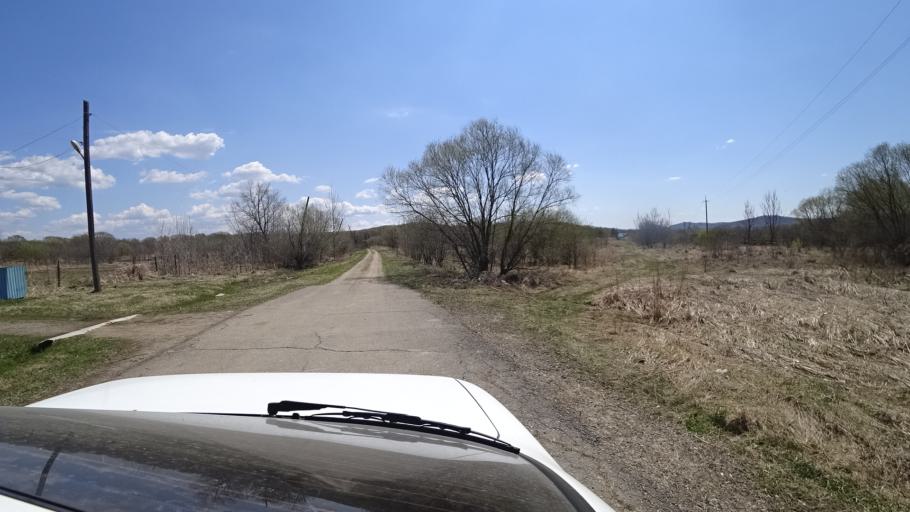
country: RU
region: Primorskiy
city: Lazo
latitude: 45.7900
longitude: 133.7681
